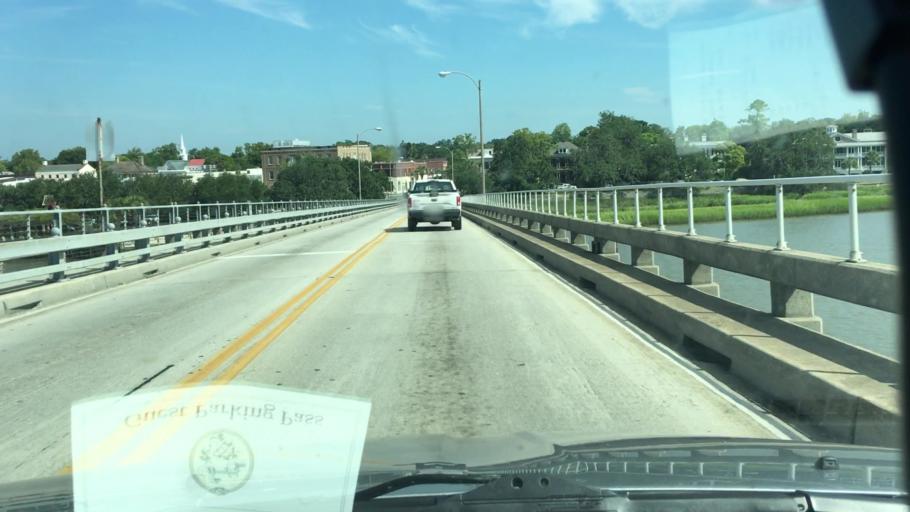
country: US
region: South Carolina
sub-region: Beaufort County
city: Beaufort
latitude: 32.4285
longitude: -80.6694
